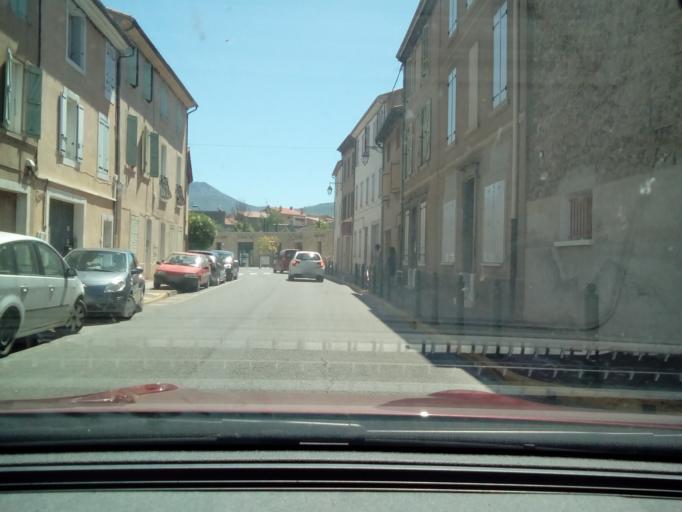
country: FR
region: Provence-Alpes-Cote d'Azur
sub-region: Departement des Bouches-du-Rhone
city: Trets
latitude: 43.4478
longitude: 5.6814
